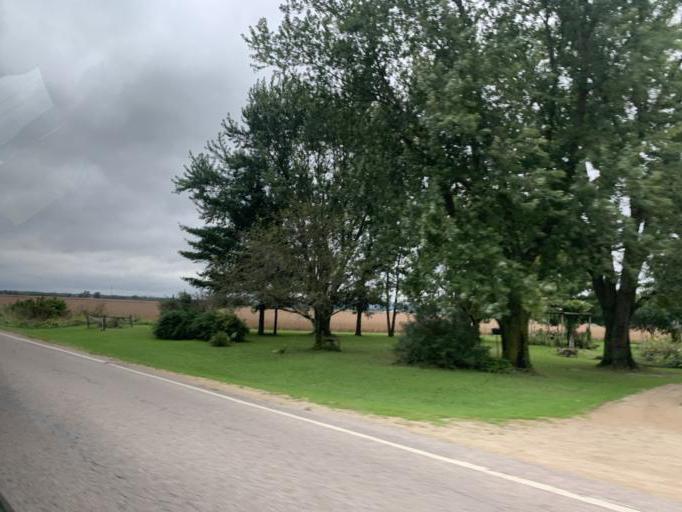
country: US
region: Wisconsin
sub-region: Sauk County
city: Spring Green
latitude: 43.1899
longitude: -90.0588
